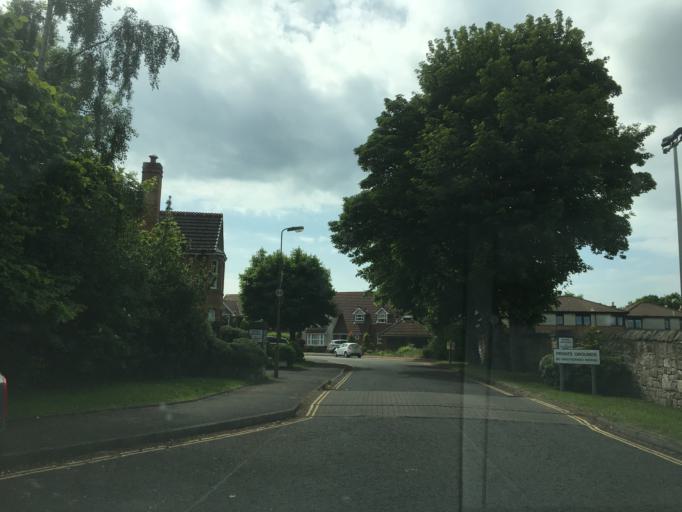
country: GB
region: Scotland
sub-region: Edinburgh
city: Colinton
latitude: 55.9251
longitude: -3.2274
